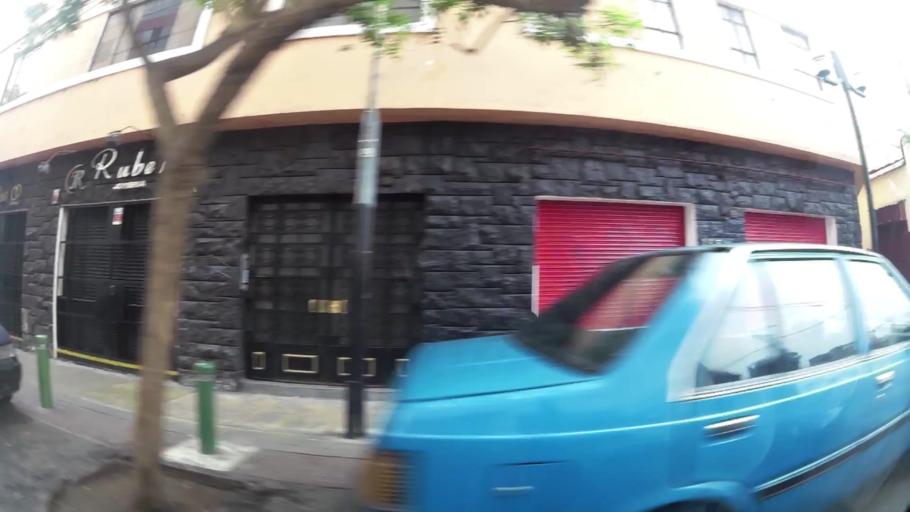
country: PE
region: Lima
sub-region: Lima
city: San Isidro
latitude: -12.1204
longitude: -77.0278
